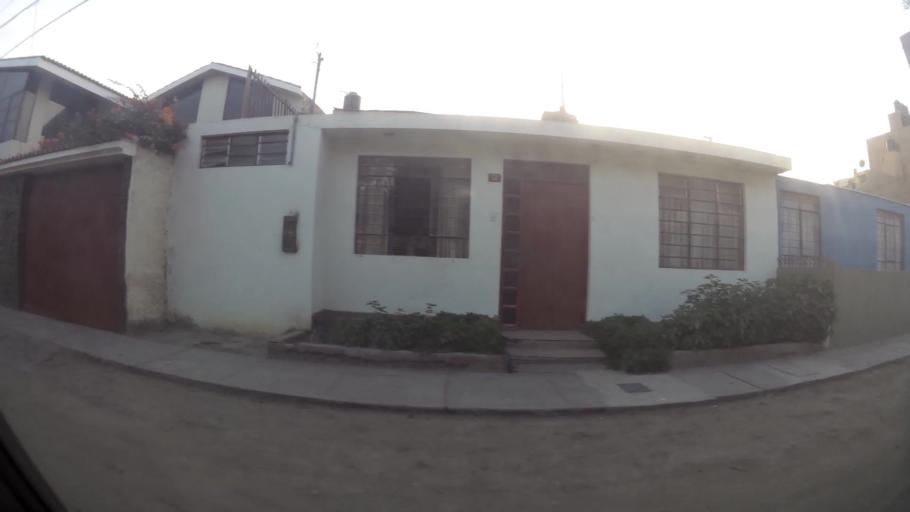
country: PE
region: Lima
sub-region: Huaura
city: Huacho
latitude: -11.1164
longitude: -77.6072
